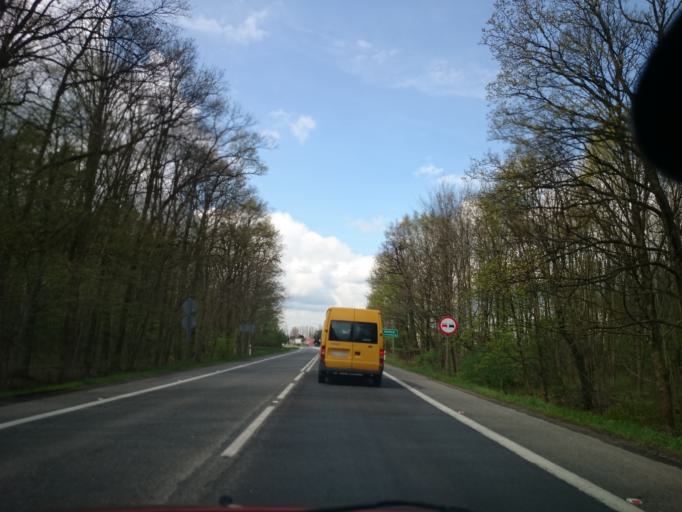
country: PL
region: Opole Voivodeship
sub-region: Powiat opolski
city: Tarnow Opolski
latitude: 50.5984
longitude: 18.0877
